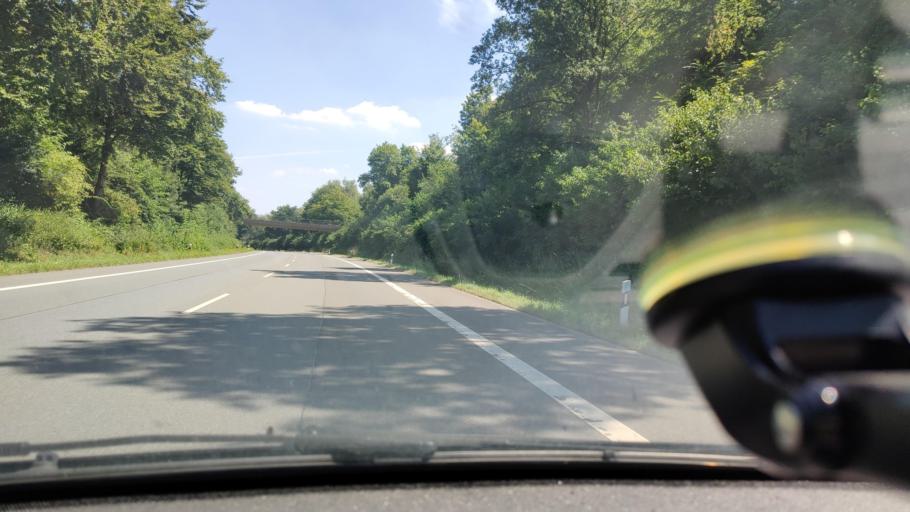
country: DE
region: North Rhine-Westphalia
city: Dorsten
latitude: 51.6525
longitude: 6.9186
